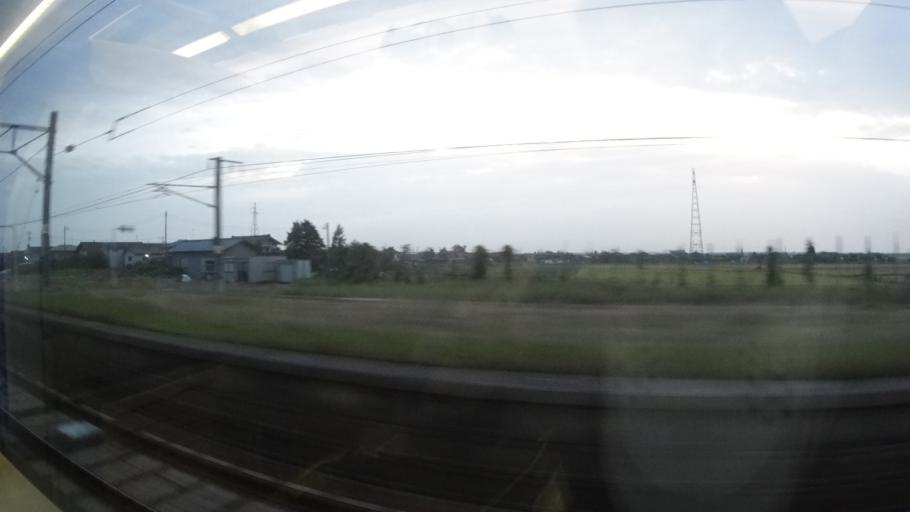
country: JP
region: Niigata
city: Shibata
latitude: 38.0212
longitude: 139.3801
